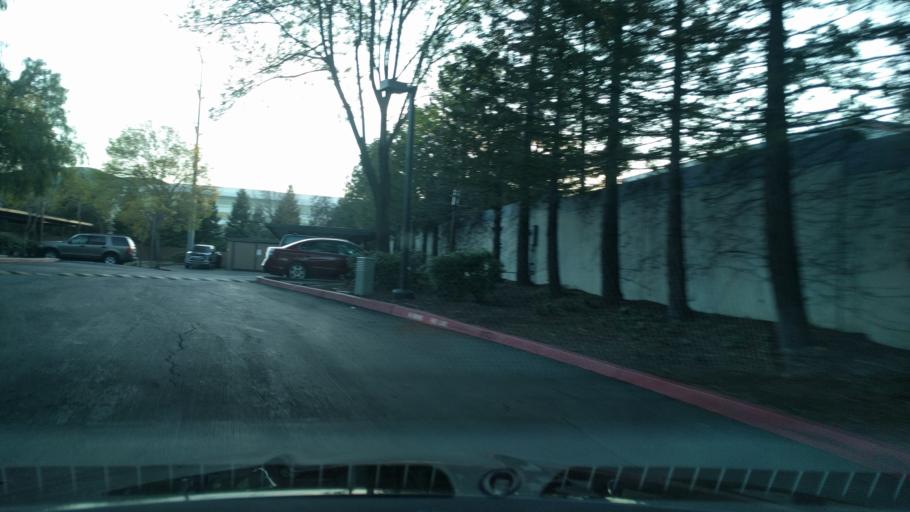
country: US
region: California
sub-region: Contra Costa County
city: San Ramon
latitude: 37.7613
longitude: -121.9518
